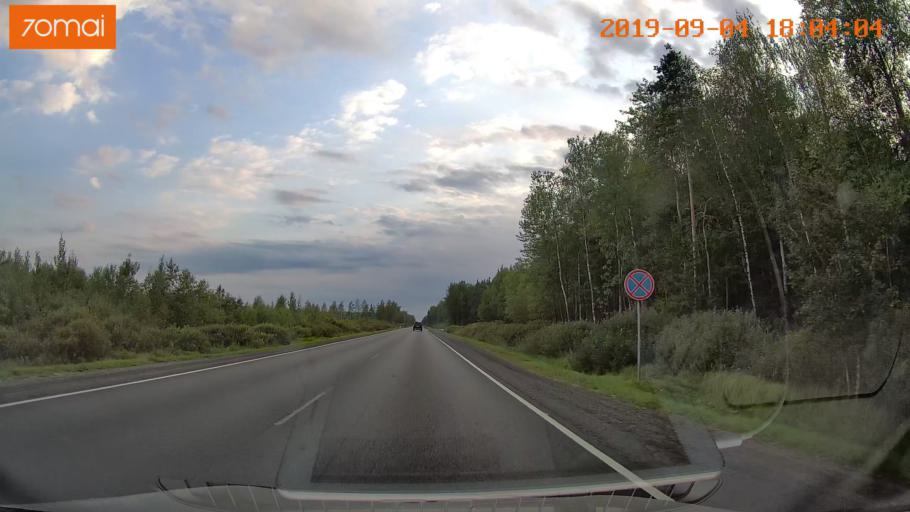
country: RU
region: Moskovskaya
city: Il'inskiy Pogost
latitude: 55.4565
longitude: 38.8440
